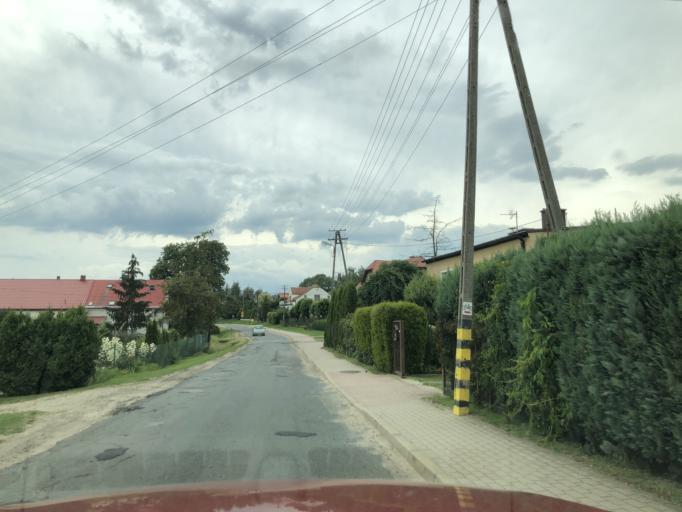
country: PL
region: Lower Silesian Voivodeship
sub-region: Powiat trzebnicki
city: Trzebnica
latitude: 51.2696
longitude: 17.0233
